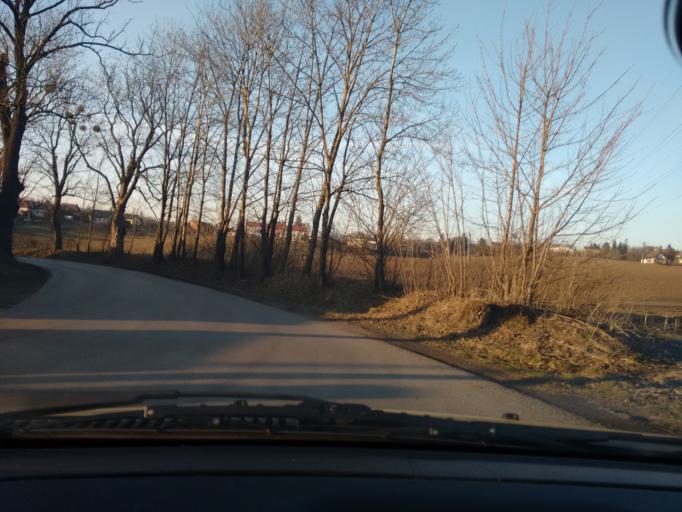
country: PL
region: Silesian Voivodeship
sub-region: Powiat cieszynski
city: Puncow
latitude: 49.7476
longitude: 18.6707
